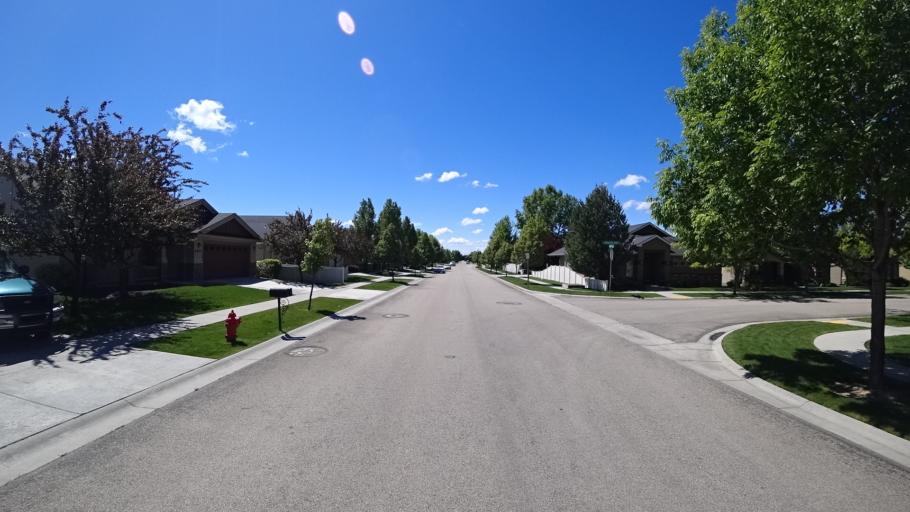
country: US
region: Idaho
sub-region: Ada County
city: Eagle
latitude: 43.6614
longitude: -116.3824
